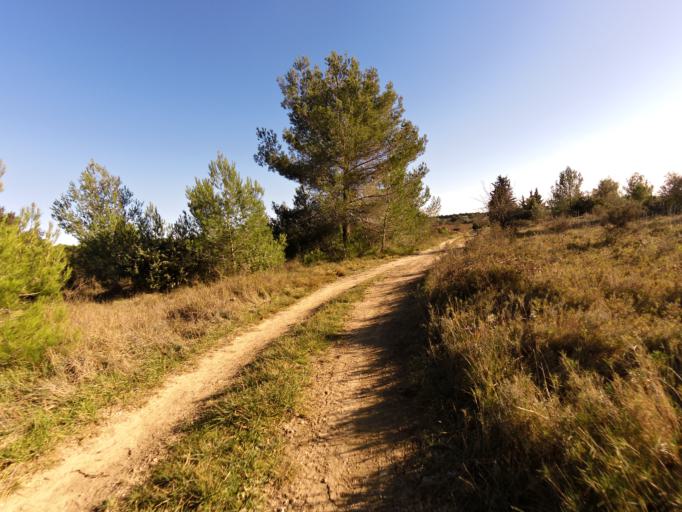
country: FR
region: Languedoc-Roussillon
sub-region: Departement du Gard
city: Gallargues-le-Montueux
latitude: 43.7327
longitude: 4.1574
